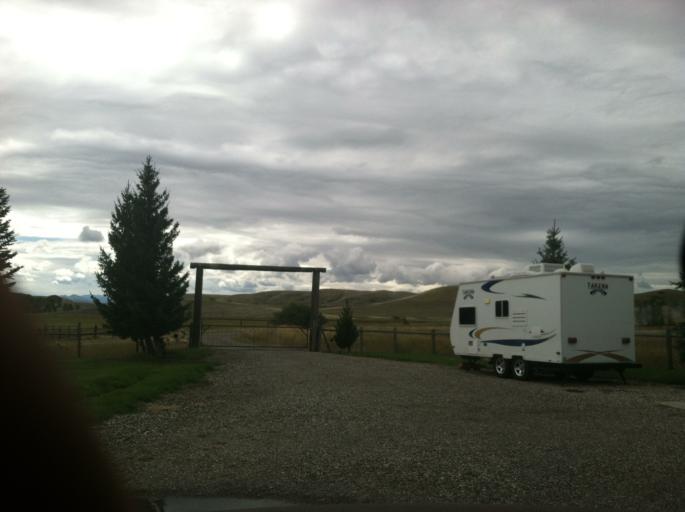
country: US
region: Montana
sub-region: Sweet Grass County
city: Big Timber
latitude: 45.8015
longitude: -109.8753
